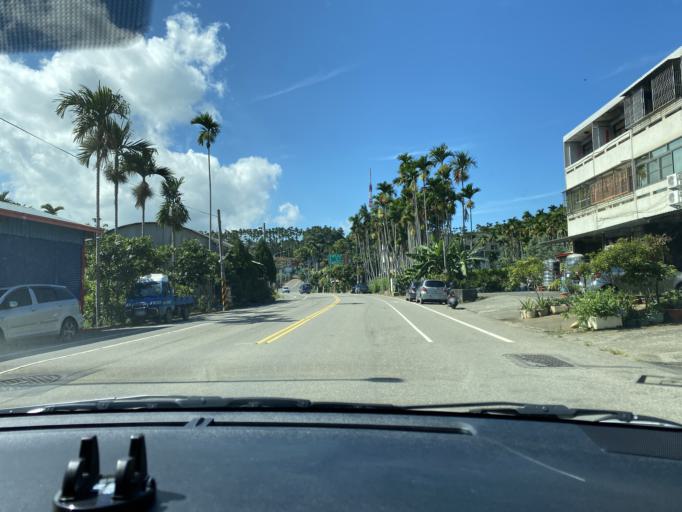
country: TW
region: Taiwan
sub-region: Nantou
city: Nantou
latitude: 23.8988
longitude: 120.6374
